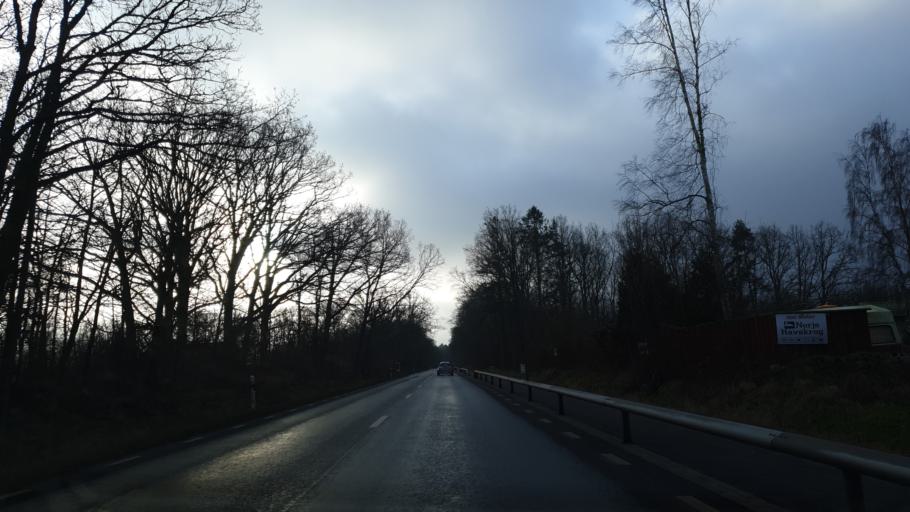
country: SE
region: Blekinge
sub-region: Karlshamns Kommun
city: Morrum
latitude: 56.1311
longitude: 14.6729
